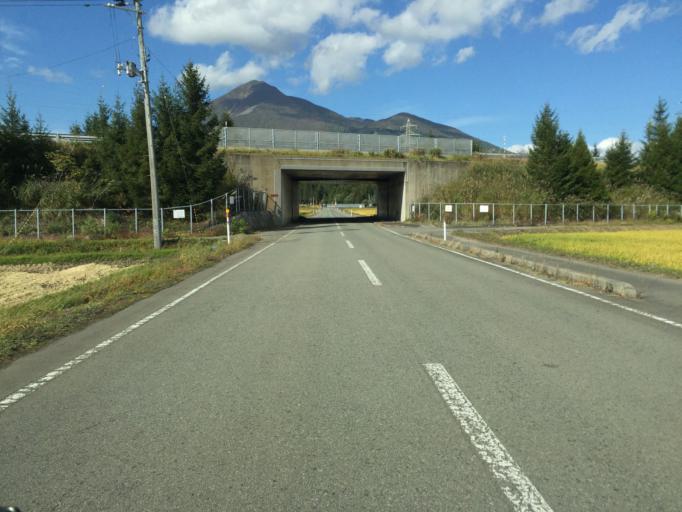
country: JP
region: Fukushima
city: Inawashiro
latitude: 37.5472
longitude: 140.0691
